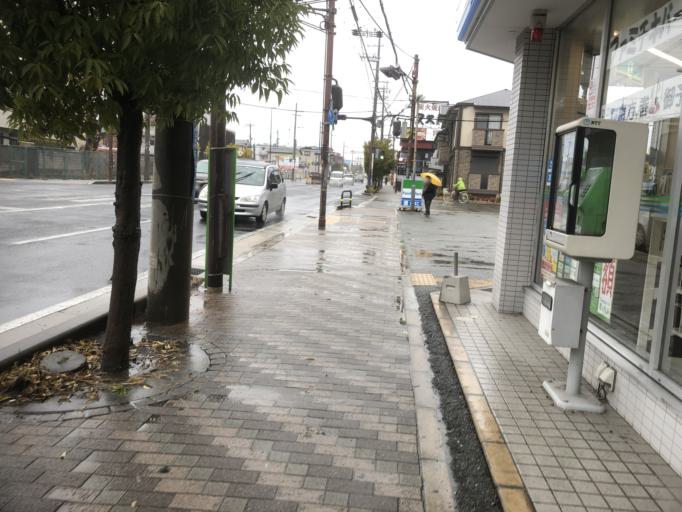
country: JP
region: Hyogo
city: Itami
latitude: 34.7540
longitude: 135.4216
